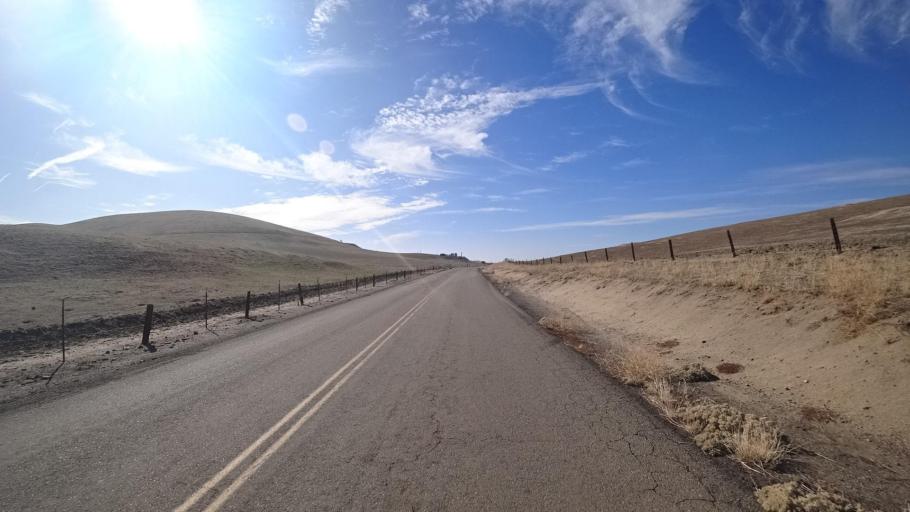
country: US
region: California
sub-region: Tulare County
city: Richgrove
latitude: 35.6349
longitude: -118.9516
